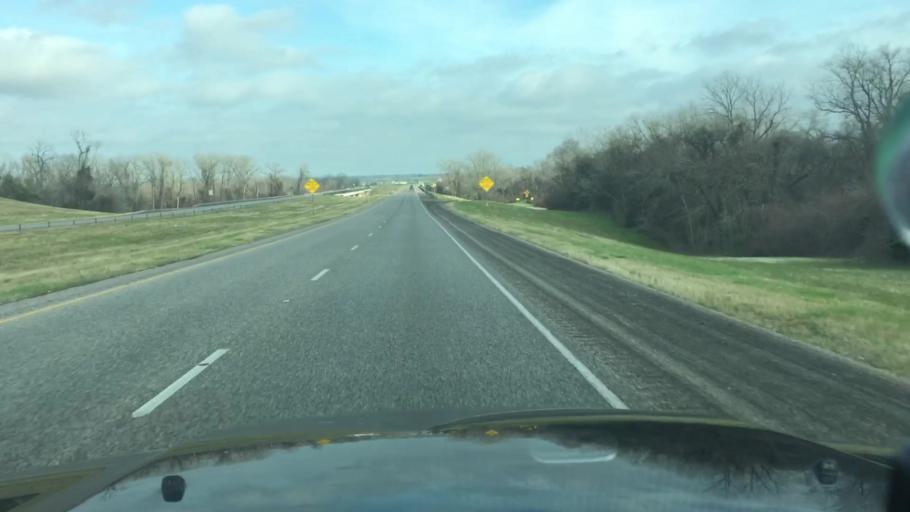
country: US
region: Texas
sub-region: Waller County
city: Hempstead
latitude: 30.1285
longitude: -96.1932
